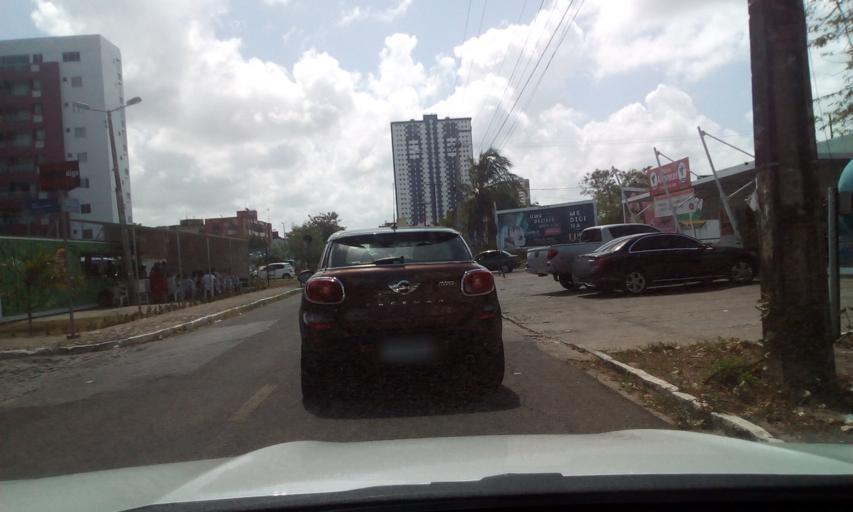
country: BR
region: Paraiba
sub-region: Joao Pessoa
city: Joao Pessoa
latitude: -7.0766
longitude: -34.8372
